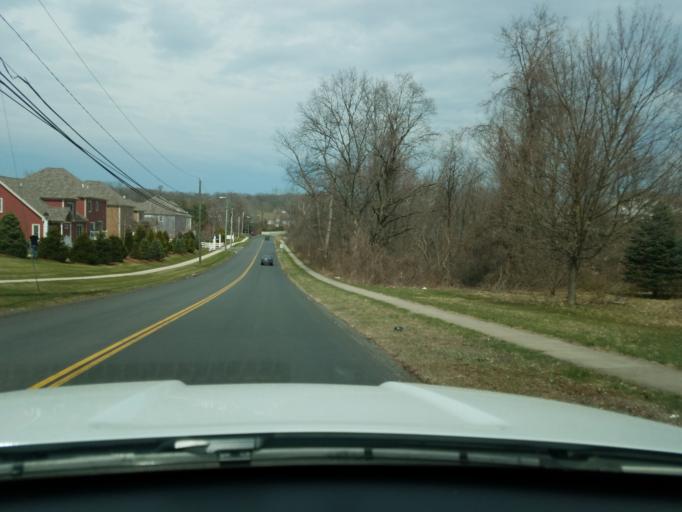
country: US
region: Connecticut
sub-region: Hartford County
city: Newington
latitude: 41.6644
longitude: -72.7167
